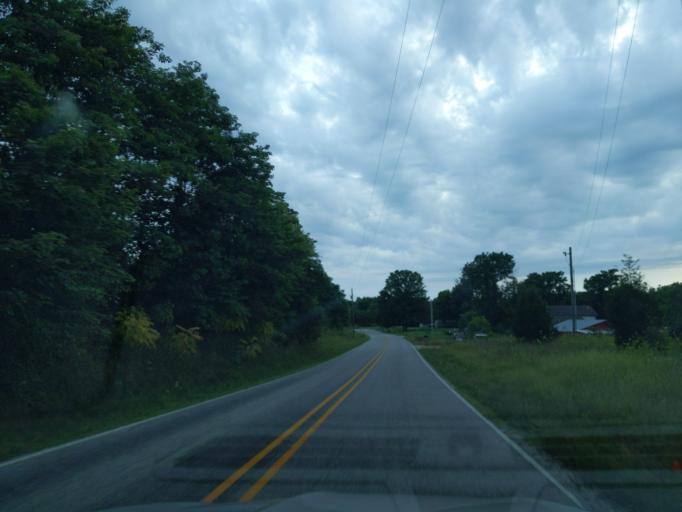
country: US
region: Indiana
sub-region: Ripley County
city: Batesville
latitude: 39.2014
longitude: -85.1980
